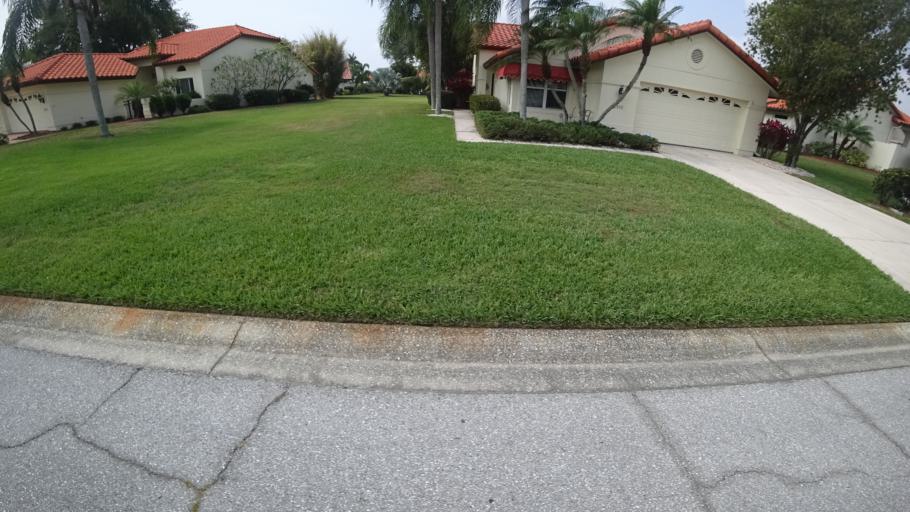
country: US
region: Florida
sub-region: Manatee County
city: Samoset
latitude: 27.4541
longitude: -82.5124
